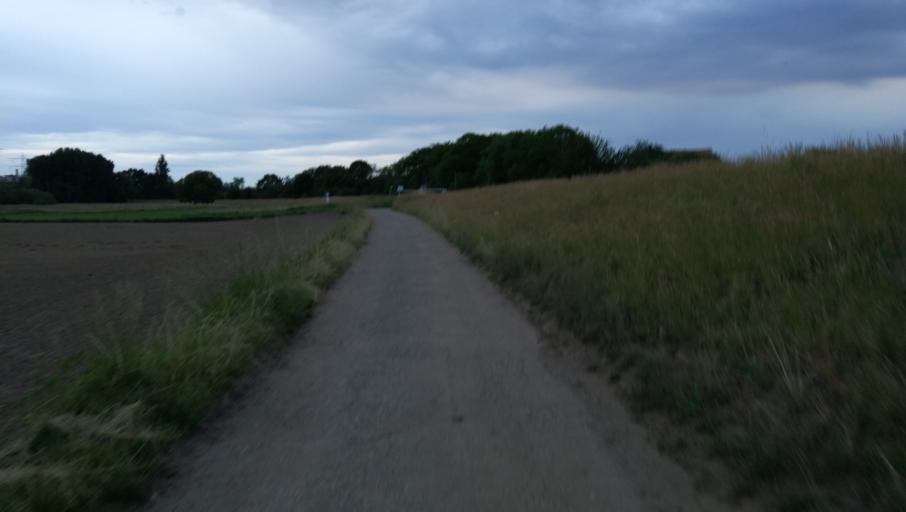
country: DE
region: Baden-Wuerttemberg
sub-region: Karlsruhe Region
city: Ketsch
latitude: 49.3431
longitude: 8.5237
